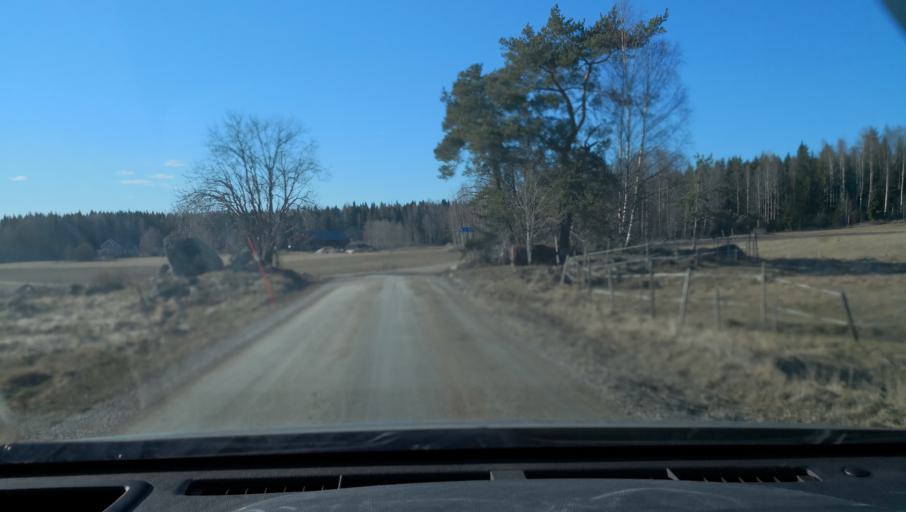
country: SE
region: Vaestmanland
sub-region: Sala Kommun
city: Sala
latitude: 60.1534
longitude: 16.6338
